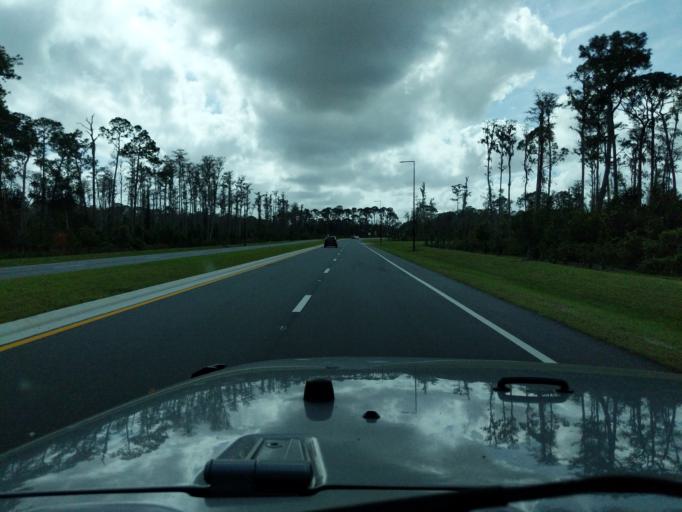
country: US
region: Florida
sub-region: Orange County
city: Bay Hill
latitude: 28.4216
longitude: -81.5897
